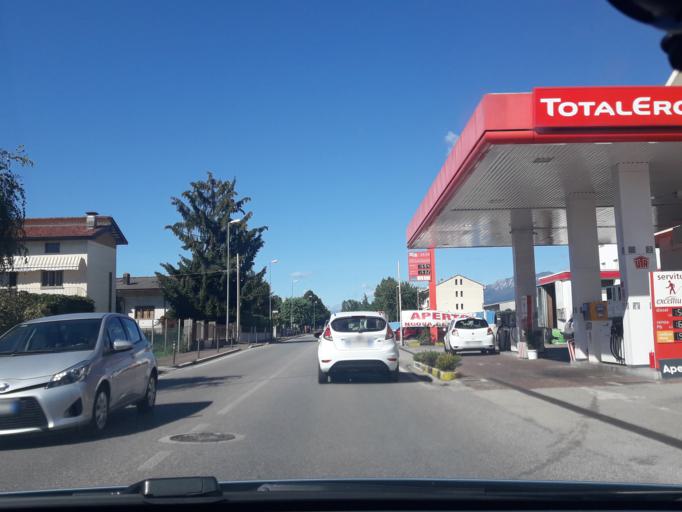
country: IT
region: Friuli Venezia Giulia
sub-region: Provincia di Udine
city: Tavagnacco
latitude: 46.1068
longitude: 13.2203
